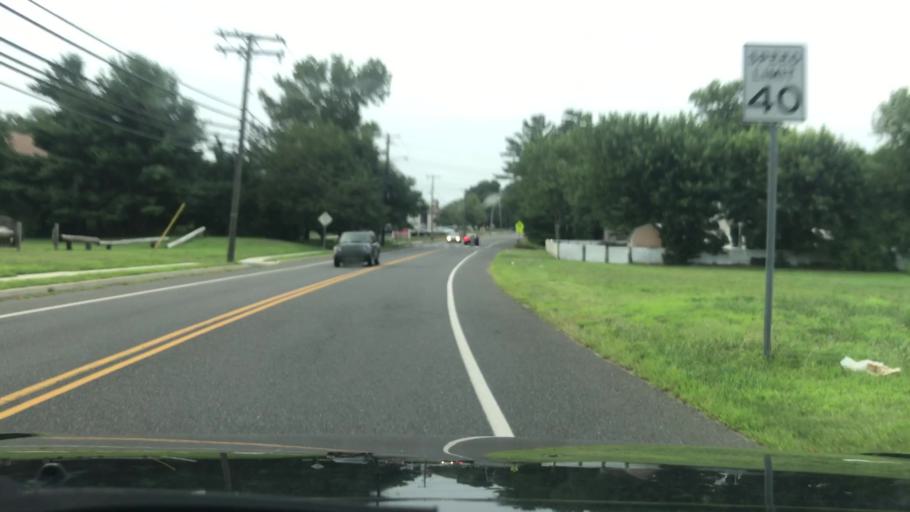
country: US
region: New Jersey
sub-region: Ocean County
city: Lakewood
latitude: 40.1224
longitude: -74.2542
